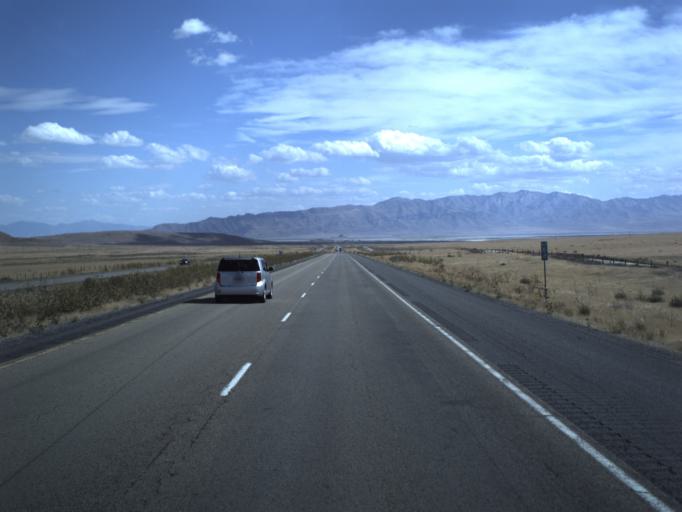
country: US
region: Utah
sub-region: Tooele County
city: Grantsville
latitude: 40.8095
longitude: -112.8671
